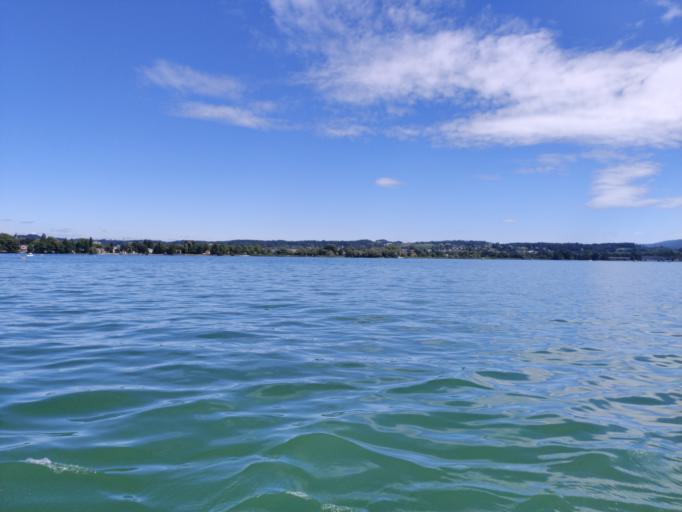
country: DE
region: Bavaria
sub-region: Swabia
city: Lindau
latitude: 47.5398
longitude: 9.6958
